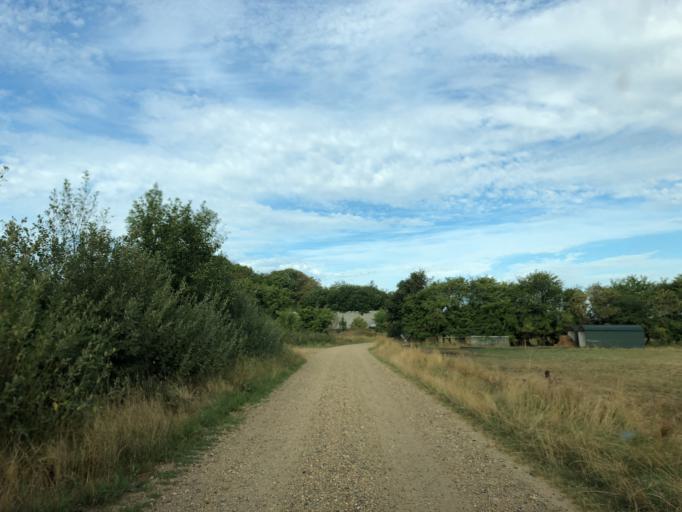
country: DK
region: Central Jutland
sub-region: Ringkobing-Skjern Kommune
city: Skjern
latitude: 56.0408
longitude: 8.4293
